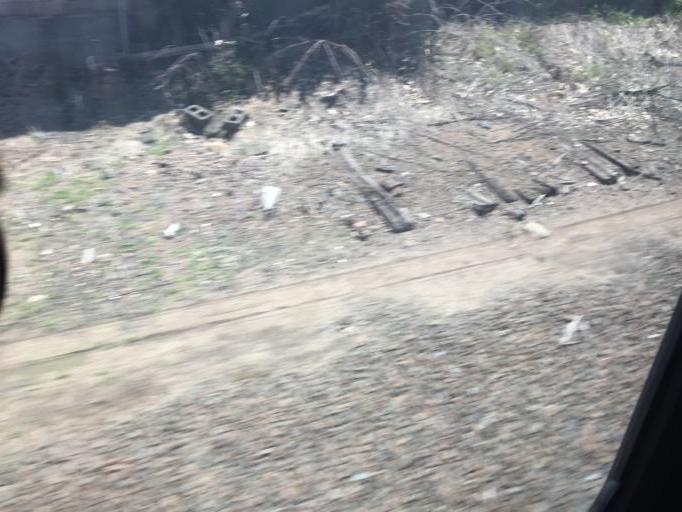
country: US
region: Connecticut
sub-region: New Haven County
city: Meriden
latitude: 41.5323
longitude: -72.8051
